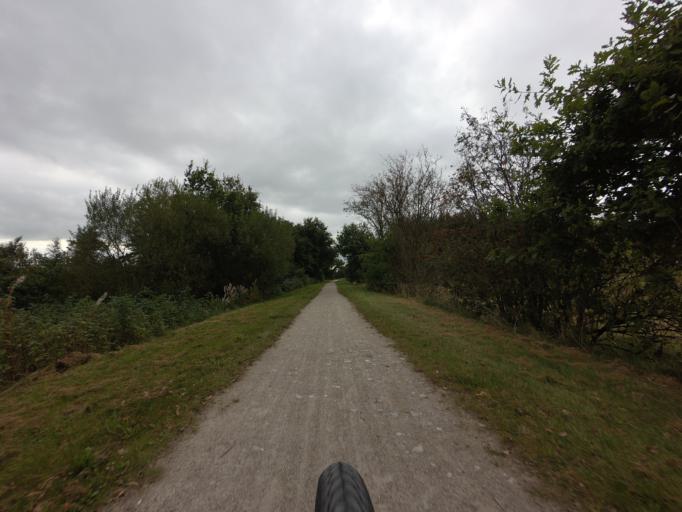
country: DK
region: Central Jutland
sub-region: Ikast-Brande Kommune
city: Brande
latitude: 55.9287
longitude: 9.1421
